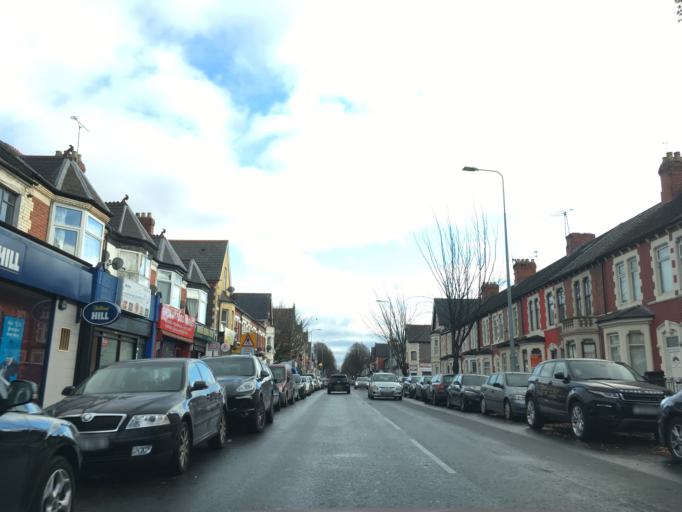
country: GB
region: Wales
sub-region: Cardiff
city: Cardiff
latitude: 51.4697
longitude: -3.1854
